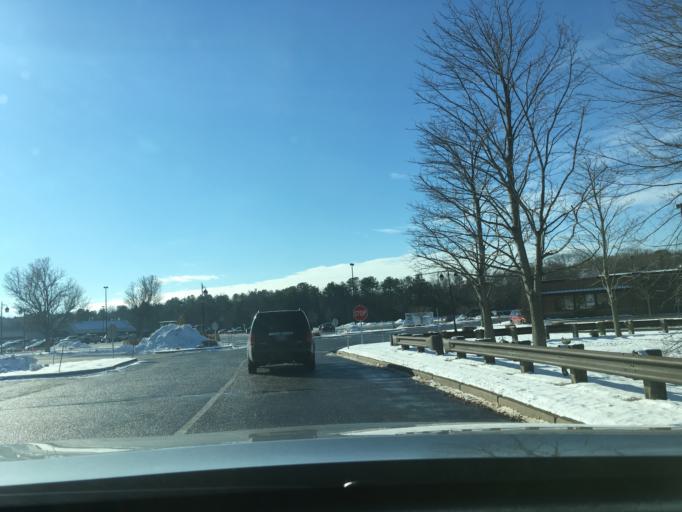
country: US
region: Rhode Island
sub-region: Kent County
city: East Greenwich
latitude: 41.6317
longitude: -71.4681
